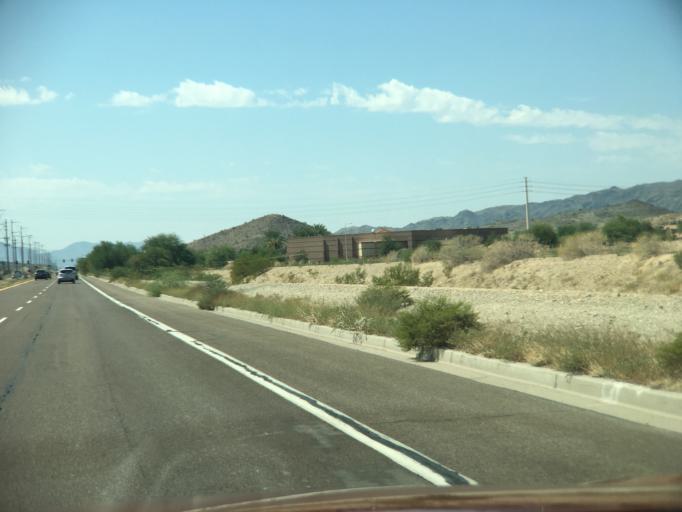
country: US
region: Arizona
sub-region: Maricopa County
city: Guadalupe
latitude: 33.2912
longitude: -112.0266
